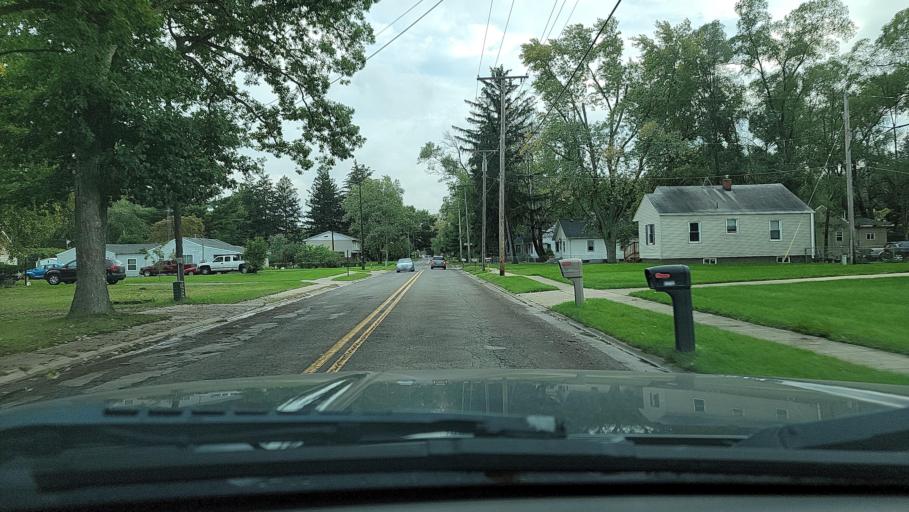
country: US
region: Indiana
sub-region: Lake County
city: Lake Station
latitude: 41.5686
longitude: -87.2170
